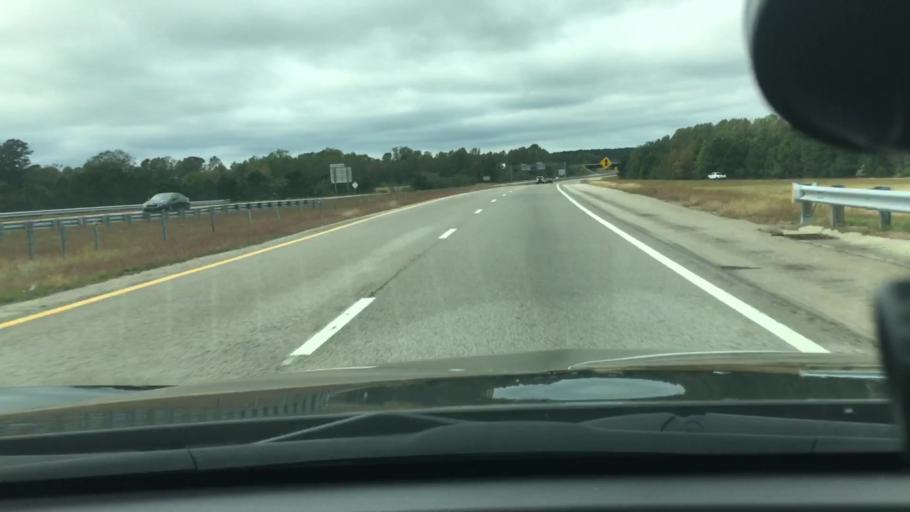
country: US
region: North Carolina
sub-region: Wilson County
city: Wilson
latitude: 35.6795
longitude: -77.9530
